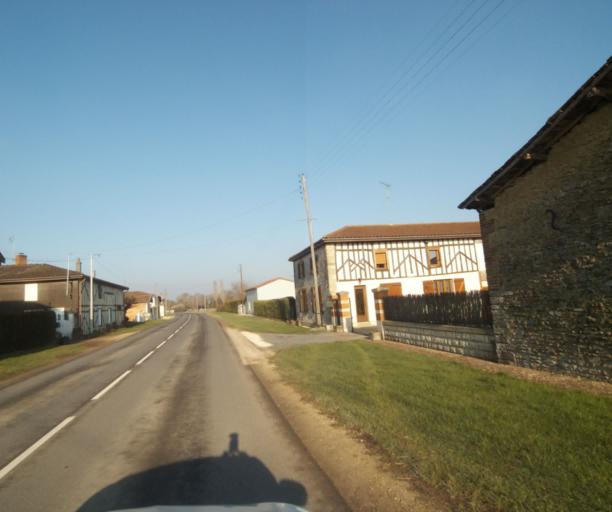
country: FR
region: Champagne-Ardenne
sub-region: Departement de la Haute-Marne
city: Montier-en-Der
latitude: 48.4595
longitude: 4.7684
